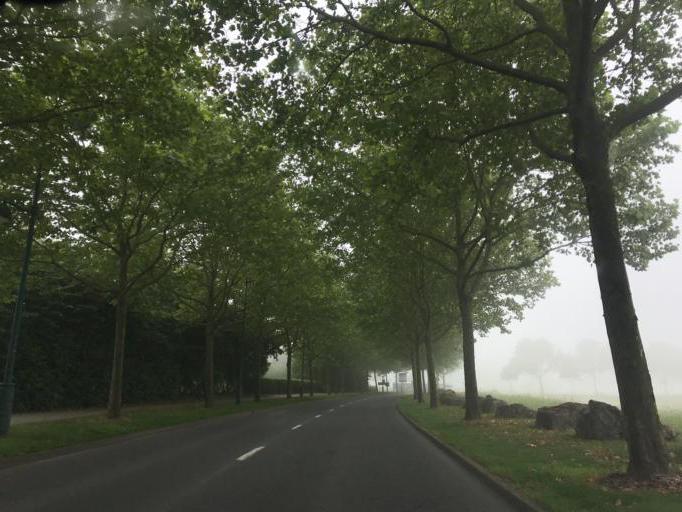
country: FR
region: Ile-de-France
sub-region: Departement de Seine-et-Marne
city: Magny-le-Hongre
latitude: 48.8760
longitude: 2.8048
